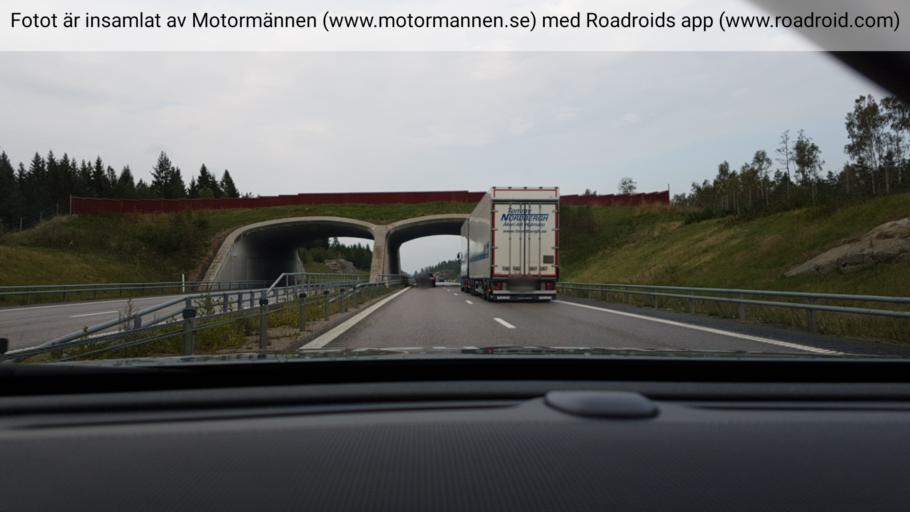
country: SE
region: Vaestra Goetaland
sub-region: Lilla Edets Kommun
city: Lodose
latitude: 58.0527
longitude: 12.1687
